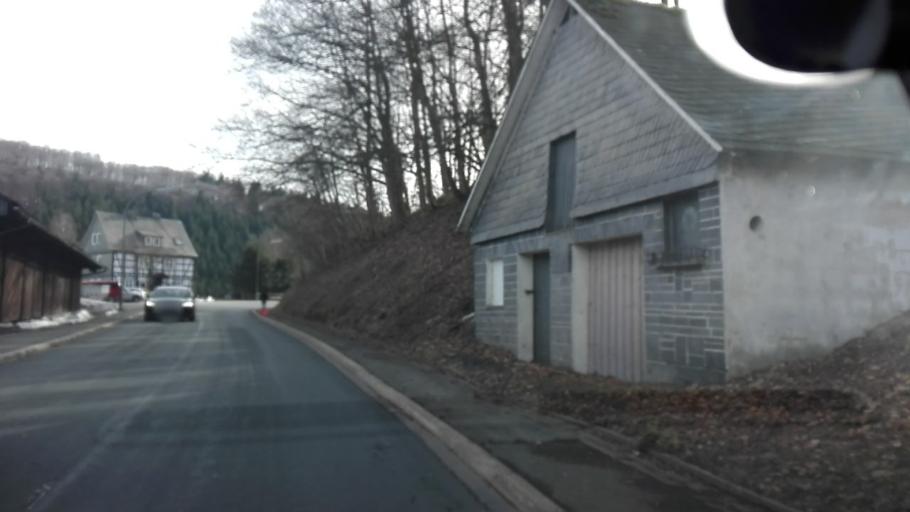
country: DE
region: North Rhine-Westphalia
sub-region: Regierungsbezirk Arnsberg
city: Winterberg
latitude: 51.1807
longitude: 8.4303
